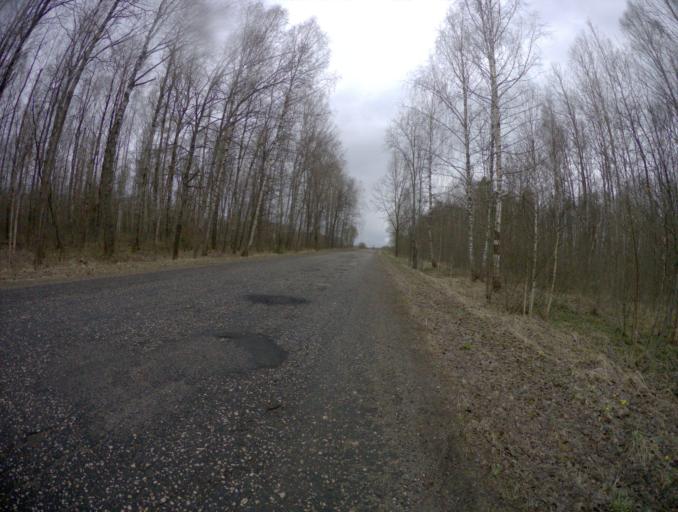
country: RU
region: Vladimir
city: Sudogda
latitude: 55.9687
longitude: 40.7023
